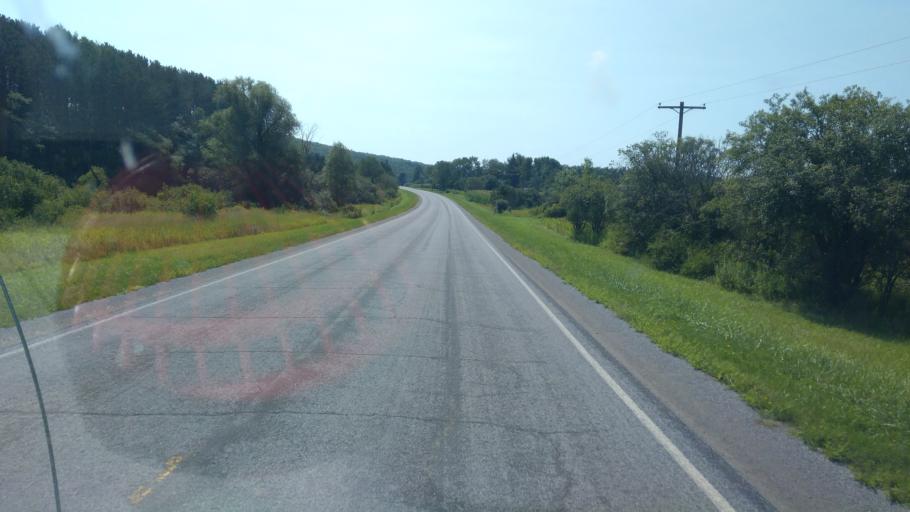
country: US
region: New York
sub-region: Allegany County
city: Belmont
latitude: 42.3364
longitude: -77.9313
